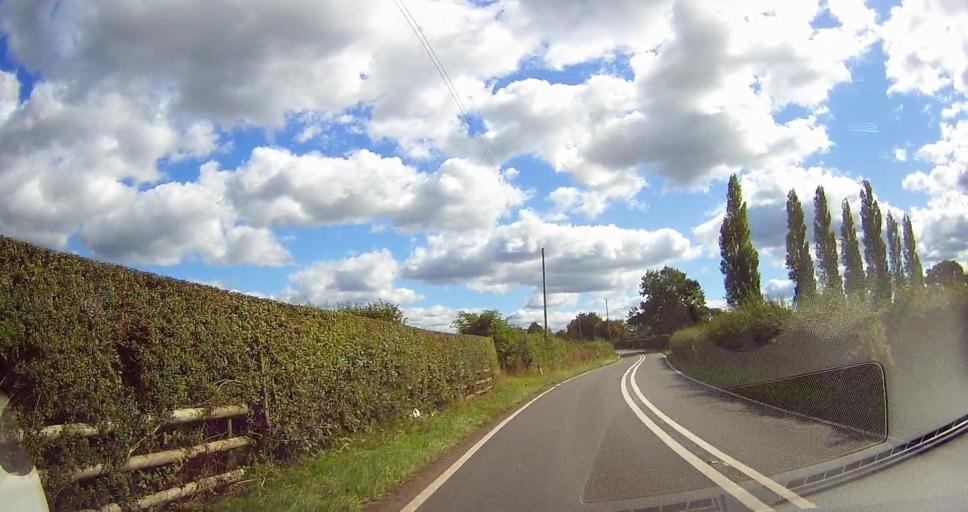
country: GB
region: England
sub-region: Cheshire East
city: Chorlton
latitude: 52.9850
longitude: -2.4543
